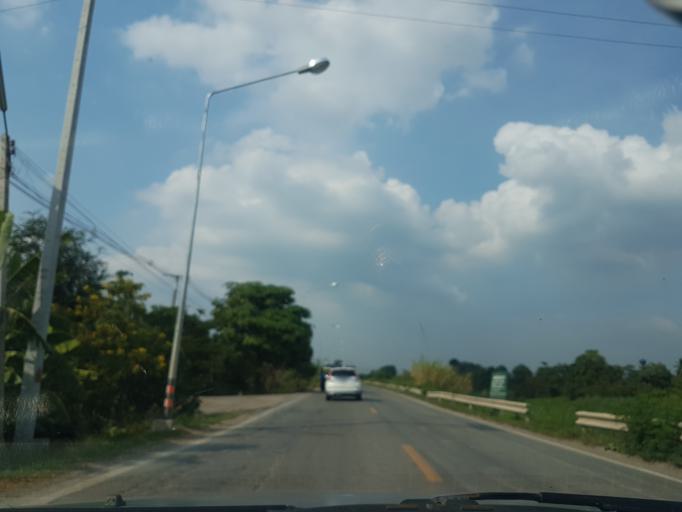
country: TH
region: Phra Nakhon Si Ayutthaya
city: Phachi
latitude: 14.4152
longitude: 100.7828
